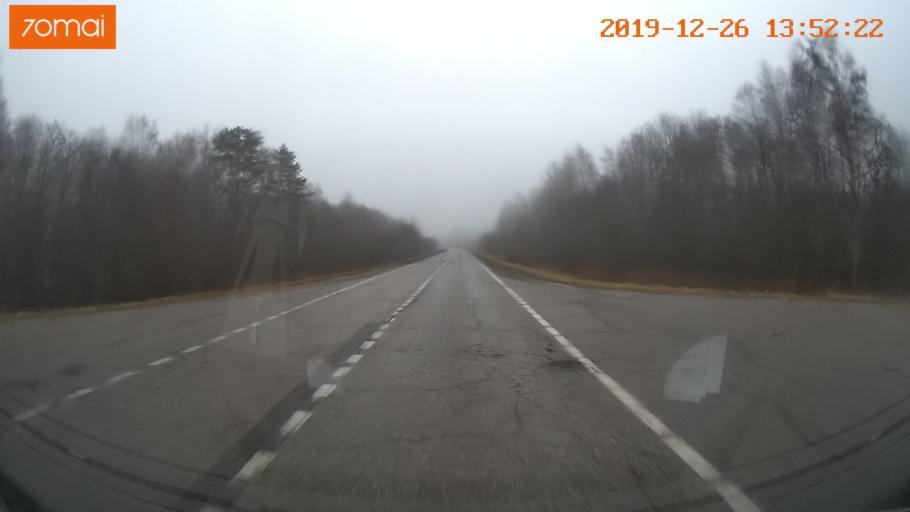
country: RU
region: Jaroslavl
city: Poshekhon'ye
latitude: 58.6326
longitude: 38.6010
